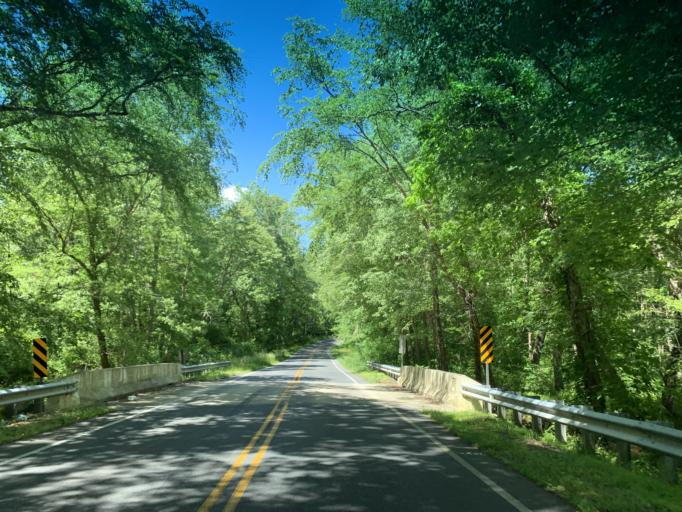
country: US
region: Maryland
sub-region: Cecil County
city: North East
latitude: 39.5686
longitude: -75.8852
